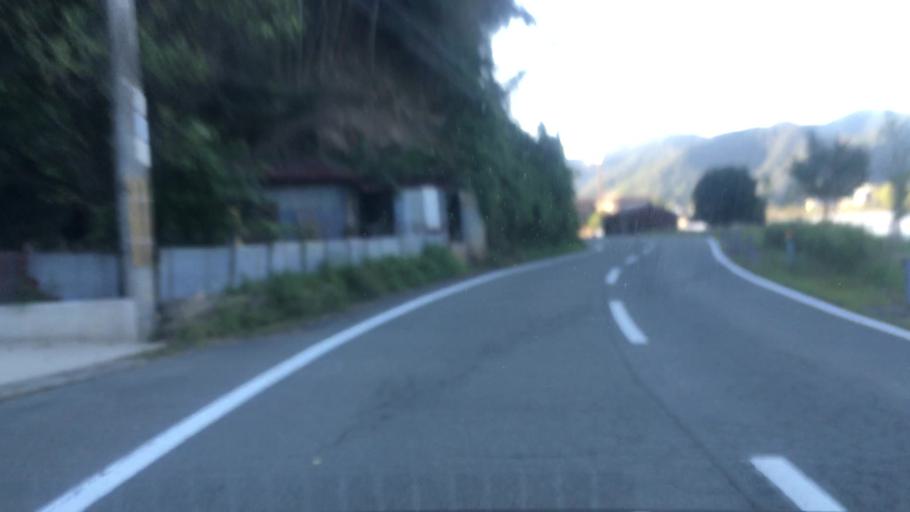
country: JP
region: Hyogo
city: Toyooka
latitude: 35.6171
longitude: 134.8232
